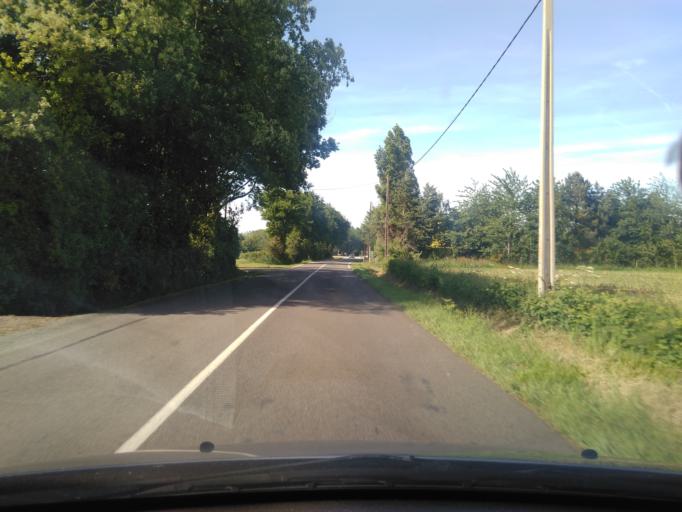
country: FR
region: Pays de la Loire
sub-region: Departement de la Vendee
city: Nieul-le-Dolent
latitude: 46.5680
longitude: -1.5110
